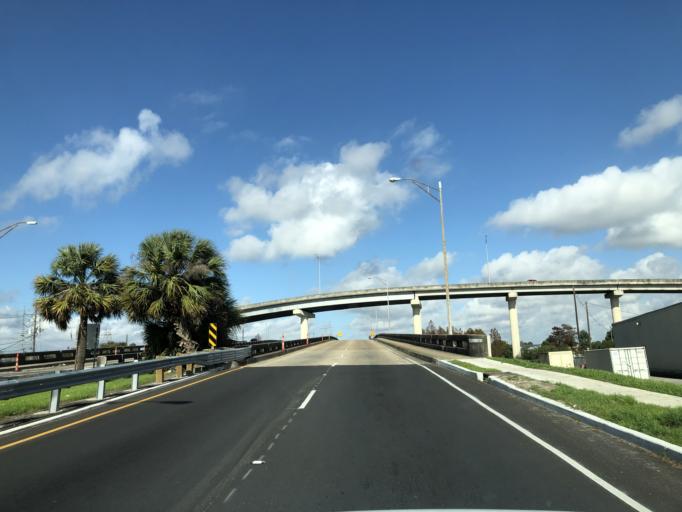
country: US
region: Louisiana
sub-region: Jefferson Parish
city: Kenner
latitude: 30.0064
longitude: -90.2209
